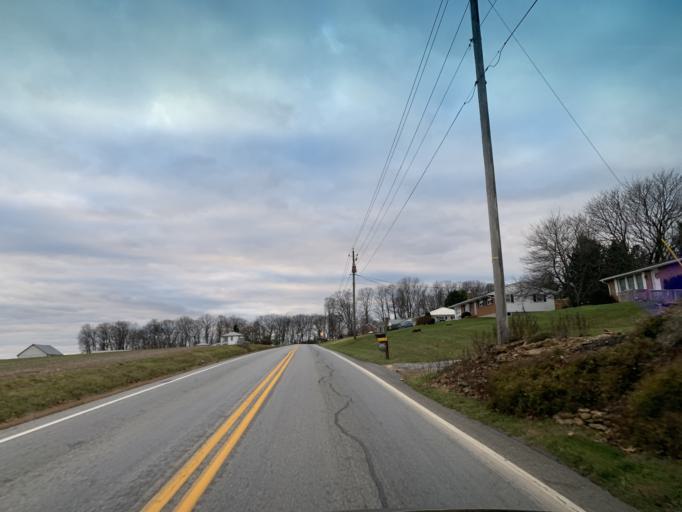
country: US
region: Pennsylvania
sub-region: York County
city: Stewartstown
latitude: 39.7738
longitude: -76.5959
